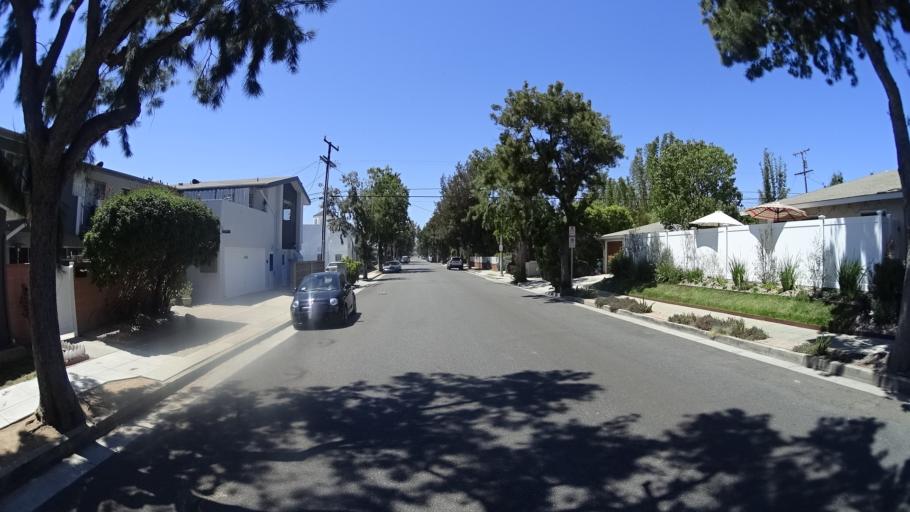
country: US
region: California
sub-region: Los Angeles County
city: Santa Monica
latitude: 34.0091
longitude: -118.4770
